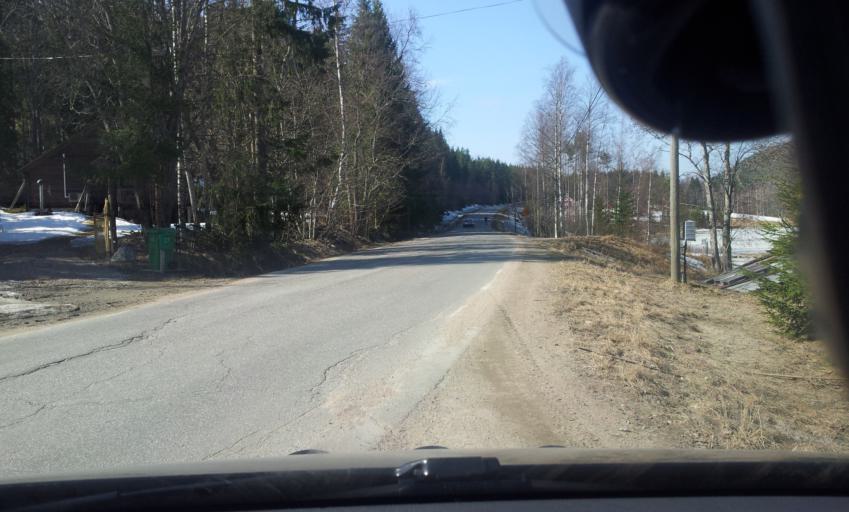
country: SE
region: Gaevleborg
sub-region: Ljusdals Kommun
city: Jaervsoe
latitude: 61.7246
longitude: 16.1495
